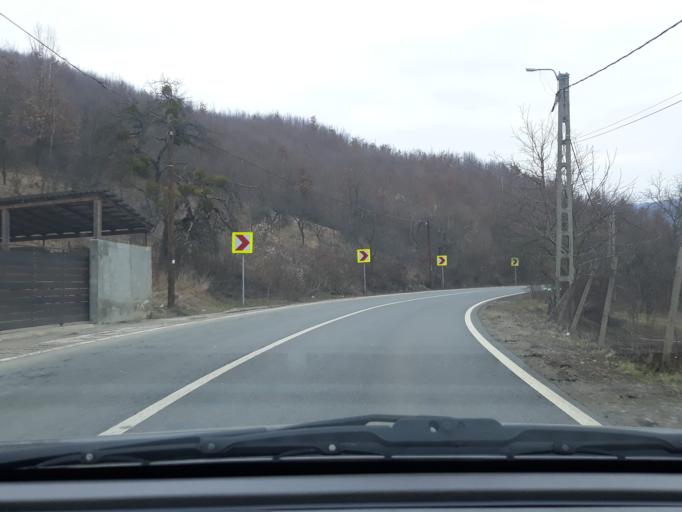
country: RO
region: Bihor
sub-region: Oras Alesd
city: Pestis
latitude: 47.0810
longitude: 22.4086
